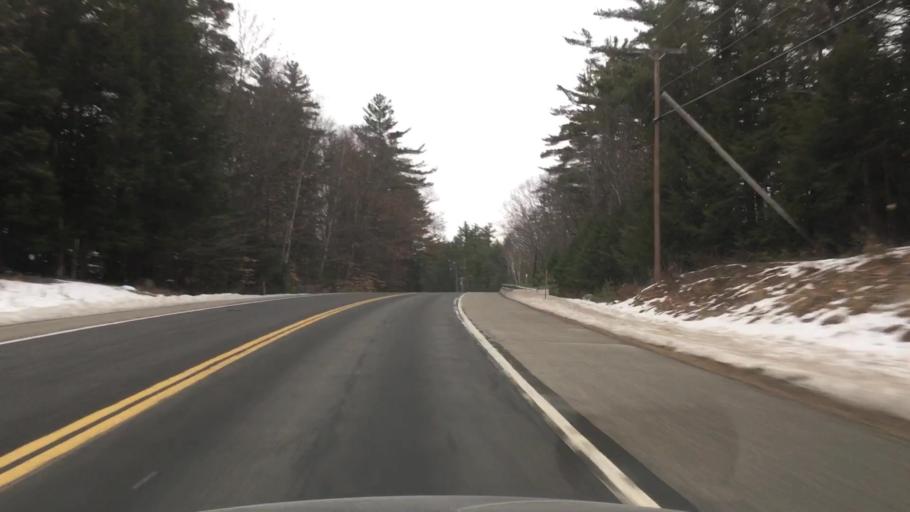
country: US
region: New Hampshire
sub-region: Merrimack County
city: Sutton
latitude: 43.2422
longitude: -71.9218
